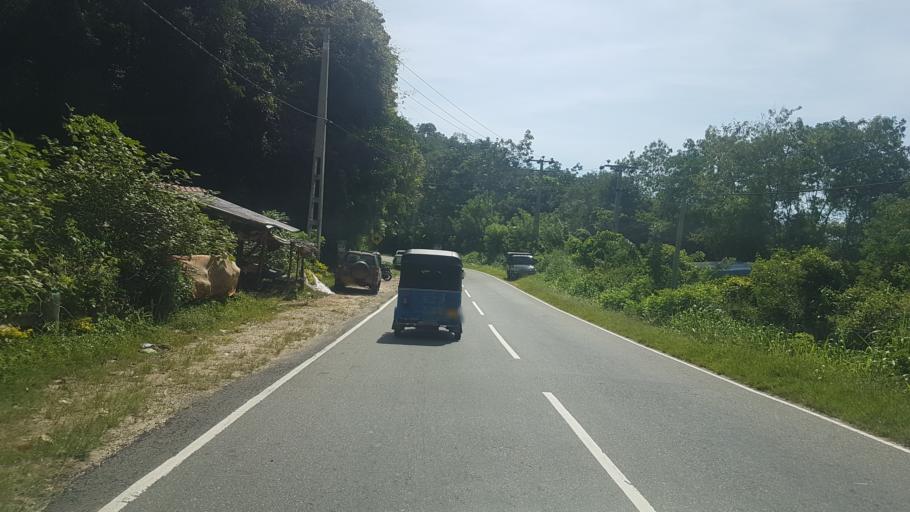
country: LK
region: Uva
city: Haputale
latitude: 6.8051
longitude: 81.0854
